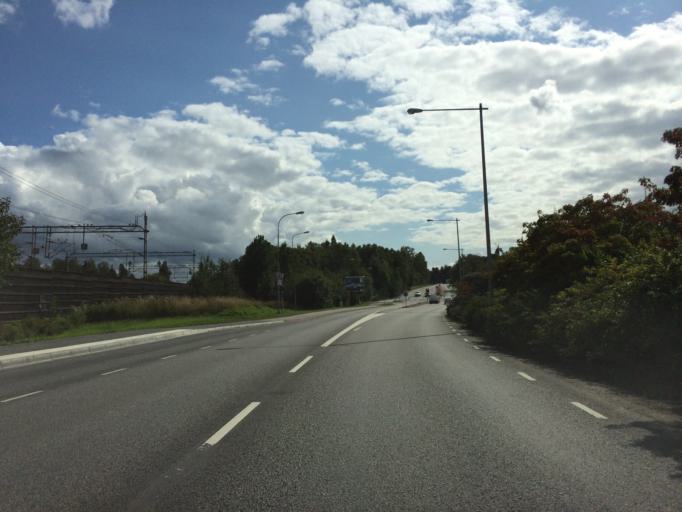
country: SE
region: Stockholm
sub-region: Sollentuna Kommun
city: Sollentuna
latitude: 59.4522
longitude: 17.9253
